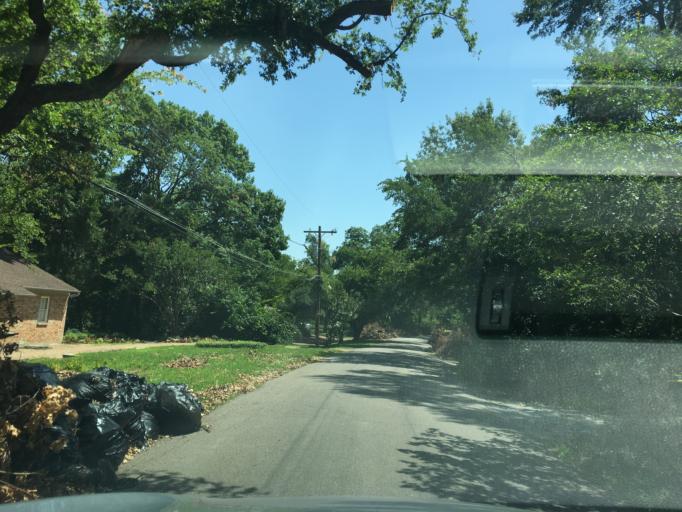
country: US
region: Texas
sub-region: Dallas County
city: University Park
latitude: 32.9068
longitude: -96.7852
